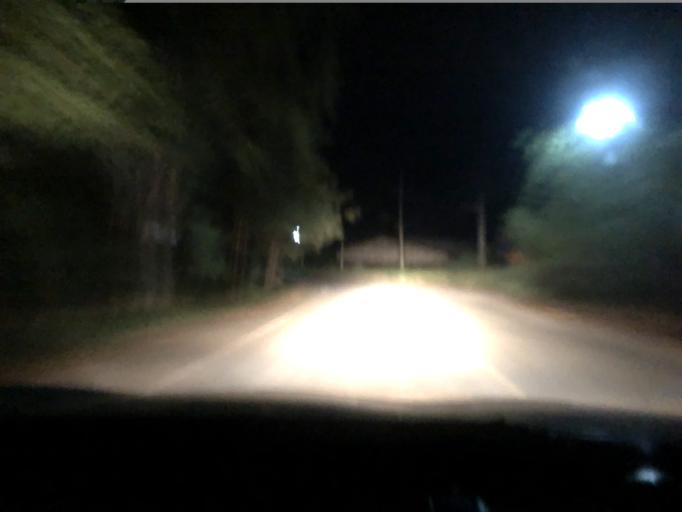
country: TH
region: Nakhon Sawan
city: Takhli
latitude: 15.2580
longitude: 100.3318
